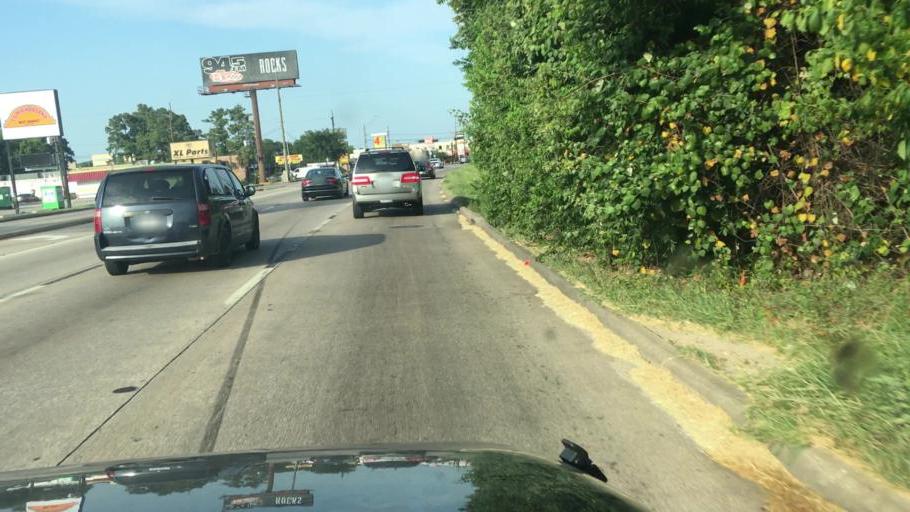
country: US
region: Texas
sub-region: Harris County
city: Spring
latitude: 30.0150
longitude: -95.4490
